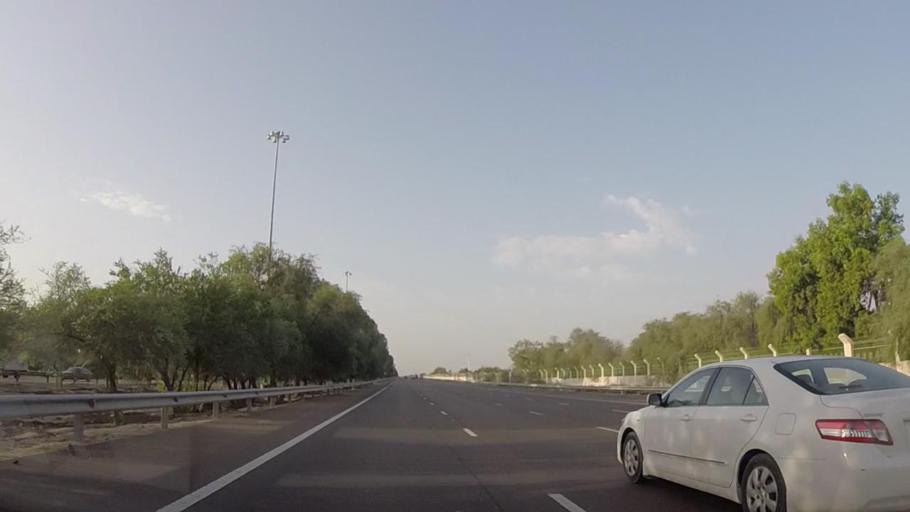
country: AE
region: Dubai
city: Dubai
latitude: 24.7623
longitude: 54.8436
